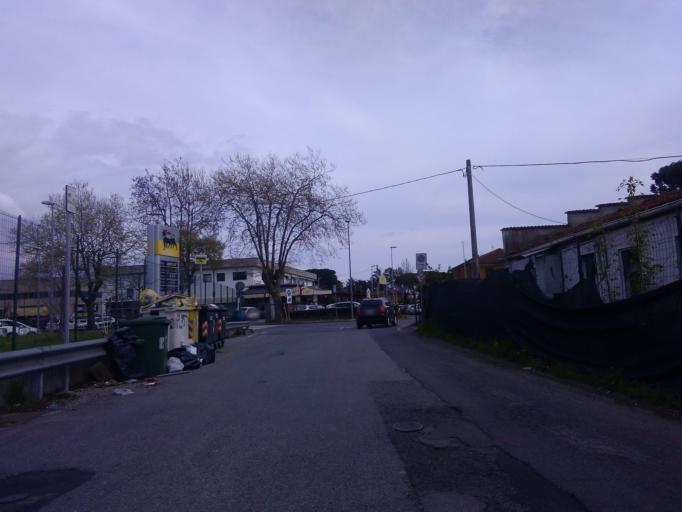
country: IT
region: Tuscany
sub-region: Provincia di Massa-Carrara
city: Marina di Carrara
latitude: 44.0530
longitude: 10.0397
